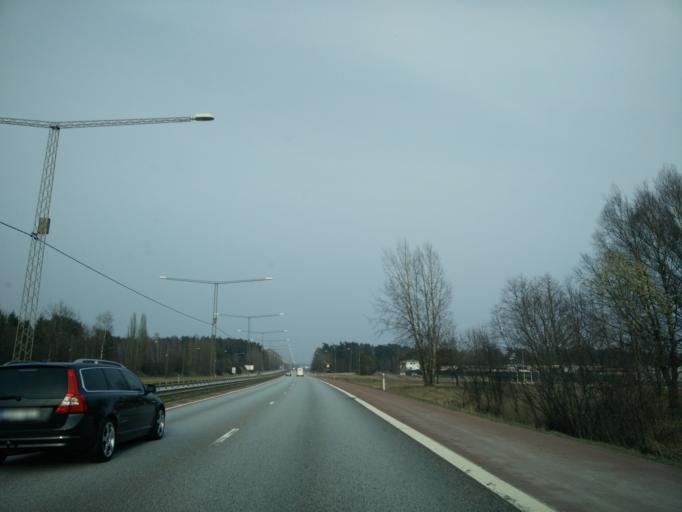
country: SE
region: Vaermland
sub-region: Hammaro Kommun
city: Skoghall
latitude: 59.3788
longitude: 13.4430
